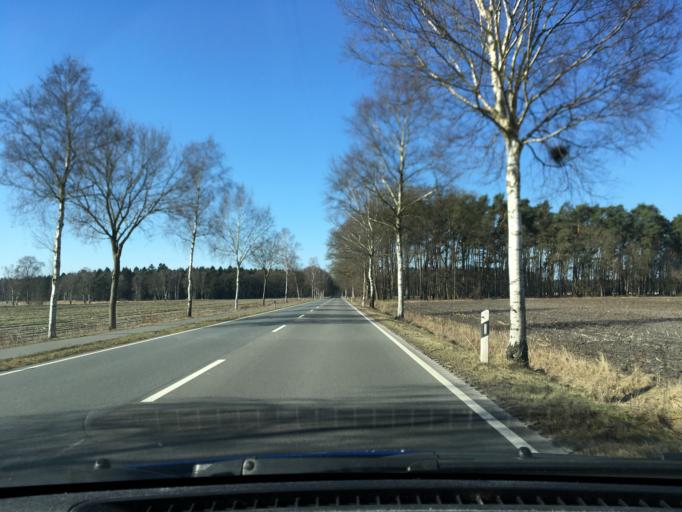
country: DE
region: Lower Saxony
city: Hemslingen
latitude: 53.0893
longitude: 9.5760
